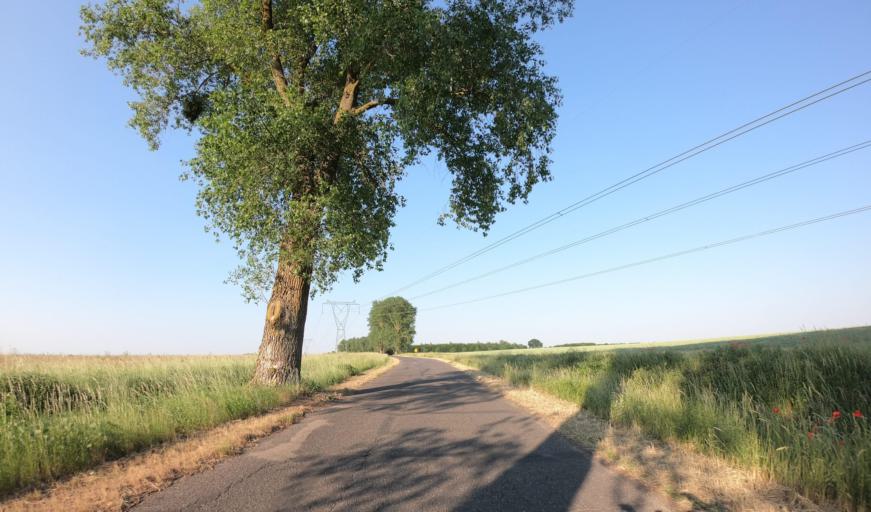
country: PL
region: West Pomeranian Voivodeship
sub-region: Powiat lobeski
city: Radowo Male
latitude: 53.6584
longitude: 15.4241
